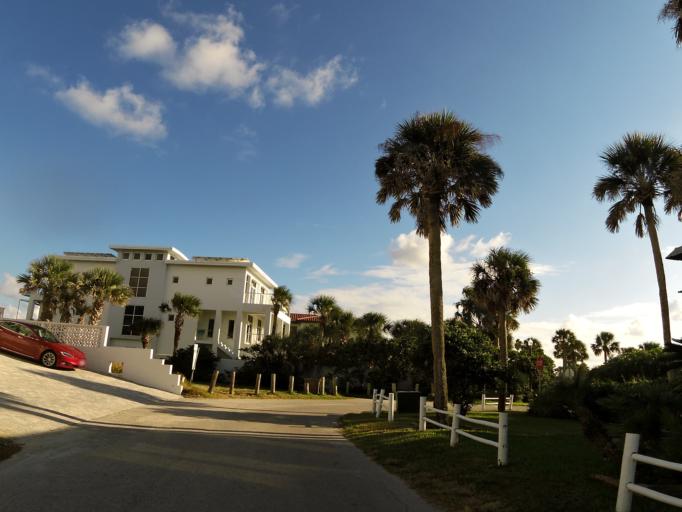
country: US
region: Florida
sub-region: Saint Johns County
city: Ponte Vedra Beach
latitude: 30.2606
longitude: -81.3831
